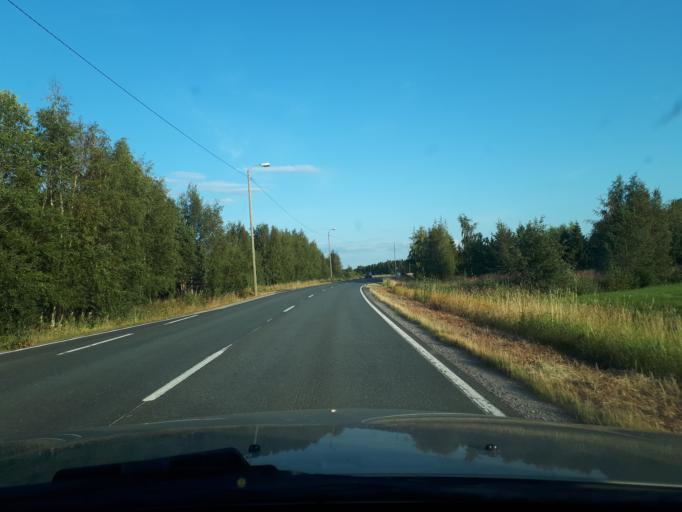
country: FI
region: Northern Ostrobothnia
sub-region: Oulu
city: Oulunsalo
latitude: 64.9832
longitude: 25.2690
